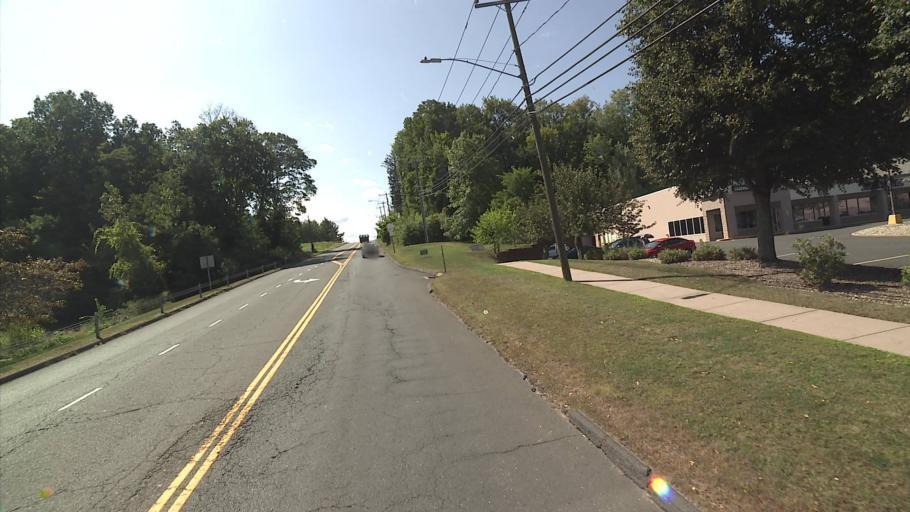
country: US
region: Connecticut
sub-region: Hartford County
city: Blue Hills
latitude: 41.8308
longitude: -72.7412
